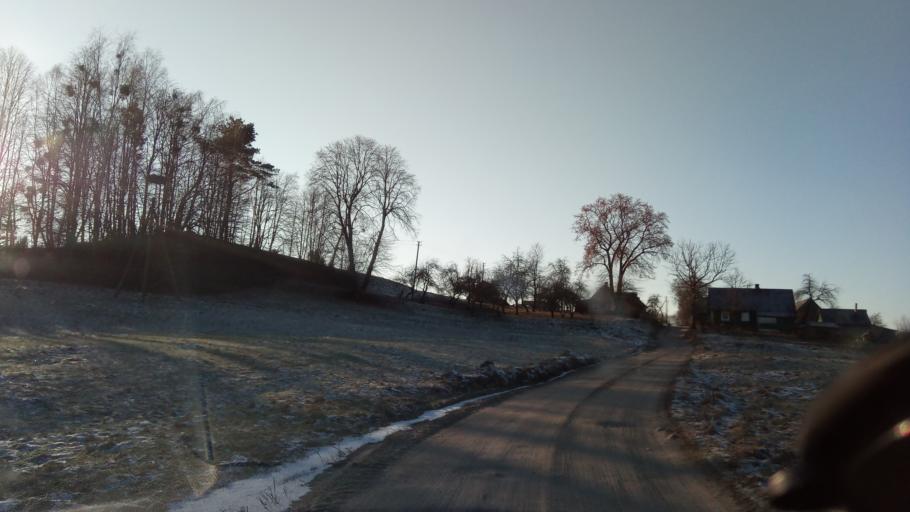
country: LT
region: Alytaus apskritis
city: Druskininkai
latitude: 54.1024
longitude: 24.0161
